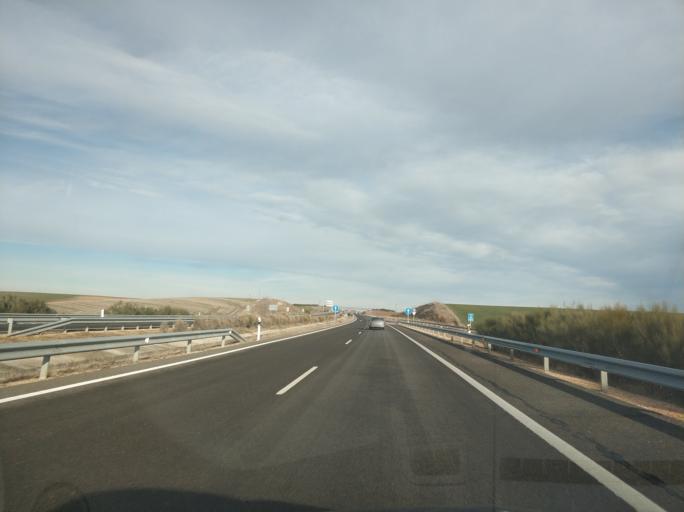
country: ES
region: Castille and Leon
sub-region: Provincia de Salamanca
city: Calzada de Valdunciel
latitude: 41.0879
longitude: -5.6904
